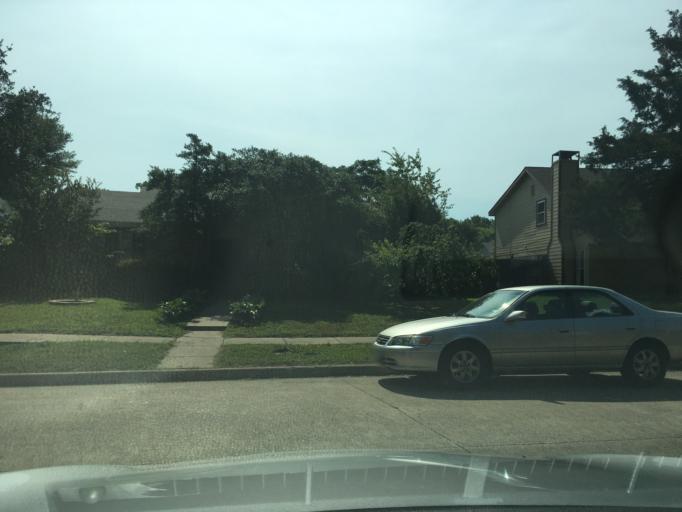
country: US
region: Texas
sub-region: Dallas County
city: Richardson
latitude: 32.9662
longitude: -96.6759
